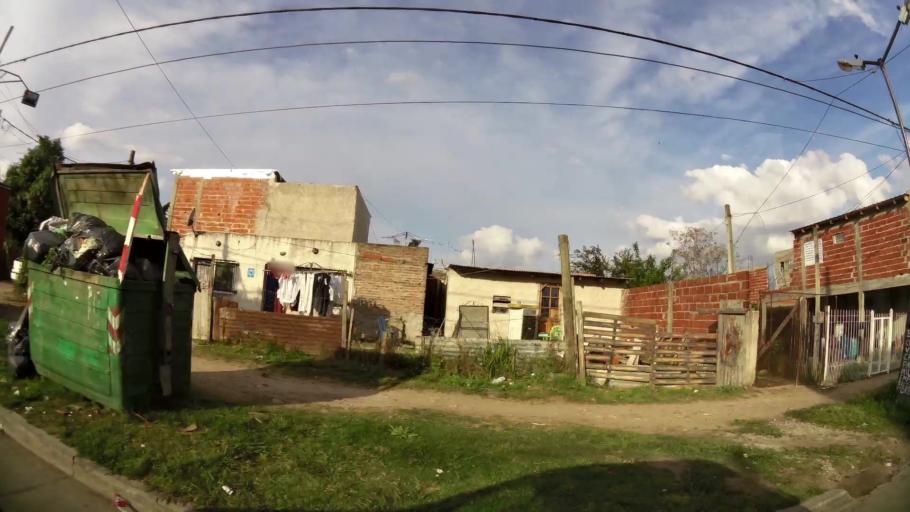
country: AR
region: Buenos Aires
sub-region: Partido de Quilmes
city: Quilmes
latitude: -34.7450
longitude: -58.2660
